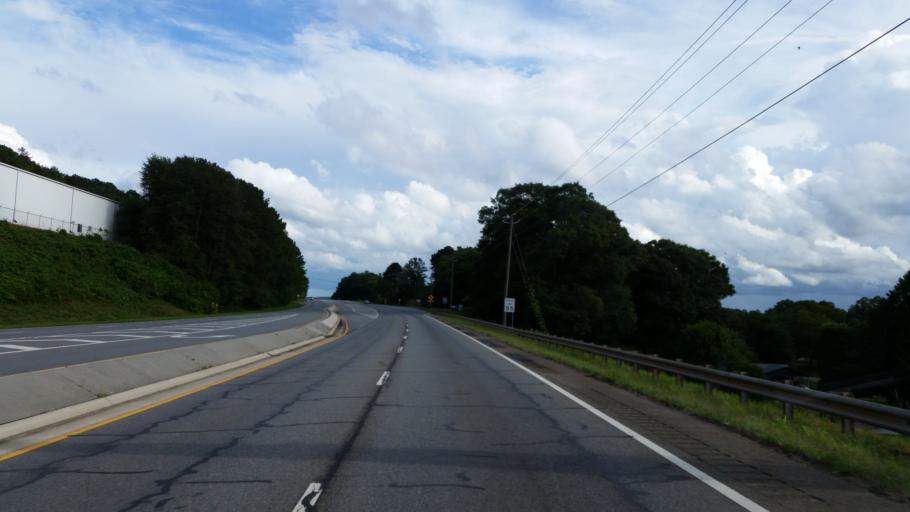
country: US
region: Georgia
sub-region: Bartow County
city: Emerson
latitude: 34.1297
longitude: -84.7521
